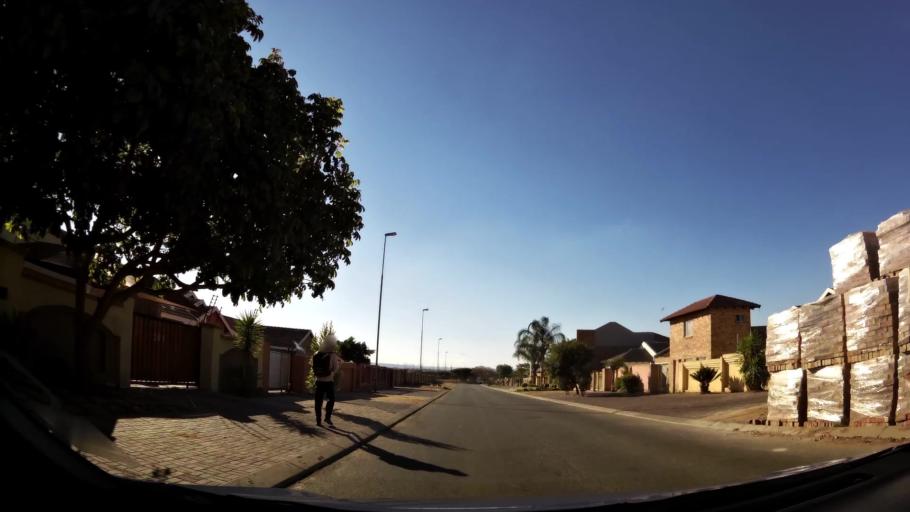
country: ZA
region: Limpopo
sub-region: Capricorn District Municipality
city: Polokwane
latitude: -23.8808
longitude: 29.4734
